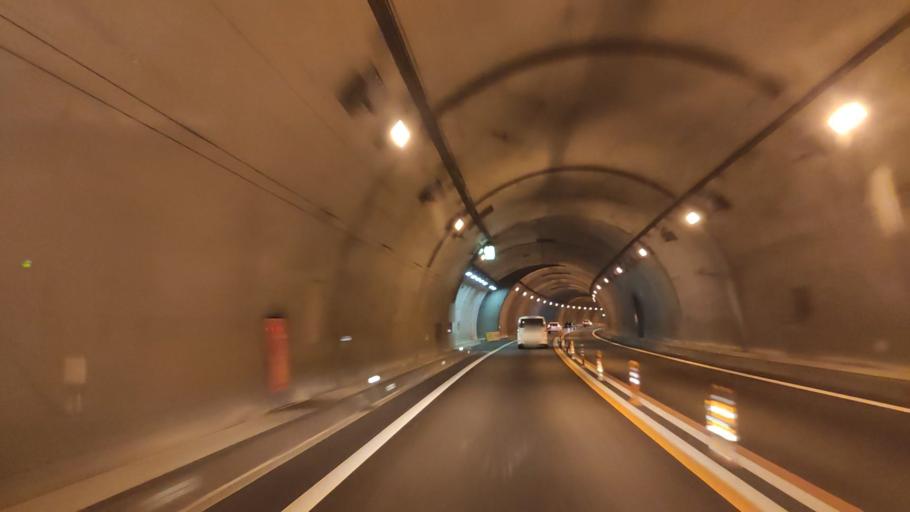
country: JP
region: Ehime
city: Kawanoecho
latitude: 33.9975
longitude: 133.6397
